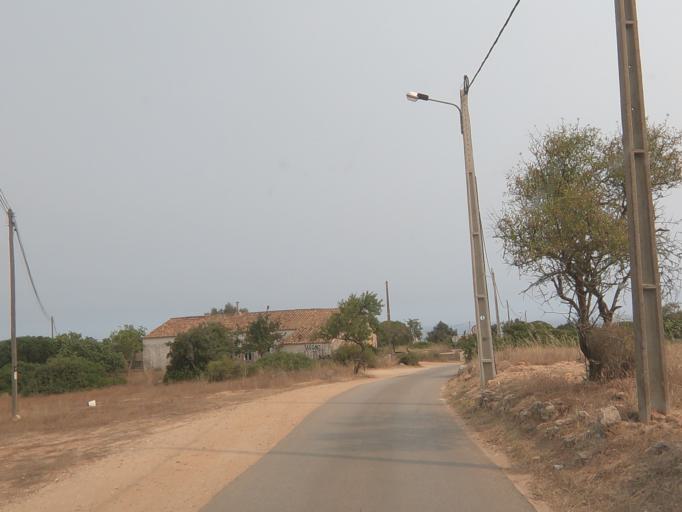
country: PT
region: Faro
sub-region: Lagoa
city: Carvoeiro
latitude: 37.0975
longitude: -8.4099
